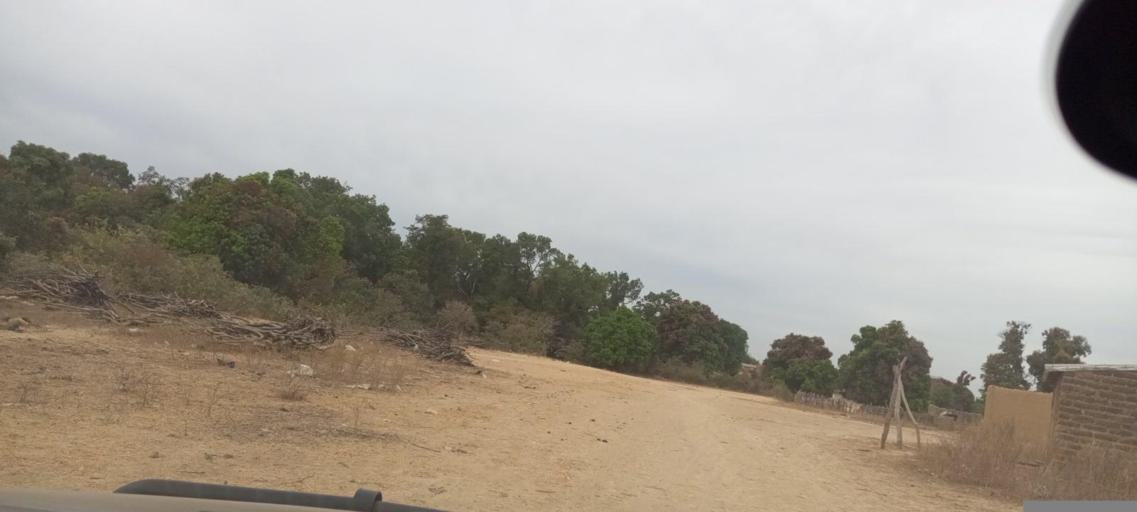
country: ML
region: Koulikoro
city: Kati
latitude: 12.7431
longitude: -8.3305
